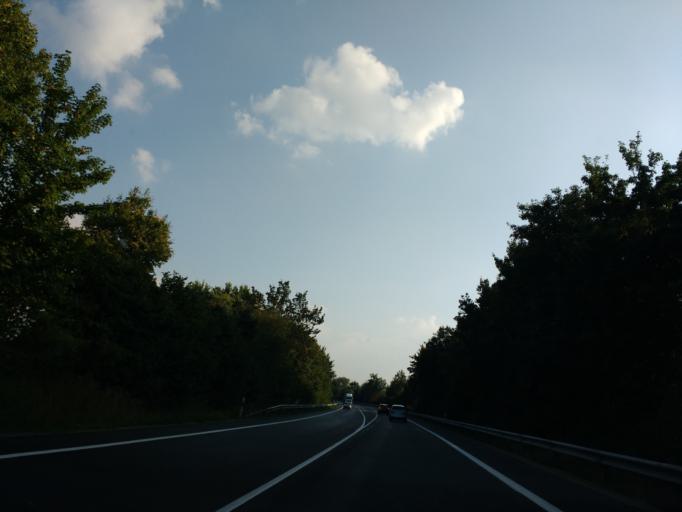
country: DE
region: North Rhine-Westphalia
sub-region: Regierungsbezirk Detmold
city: Steinheim
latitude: 51.9003
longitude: 9.0861
